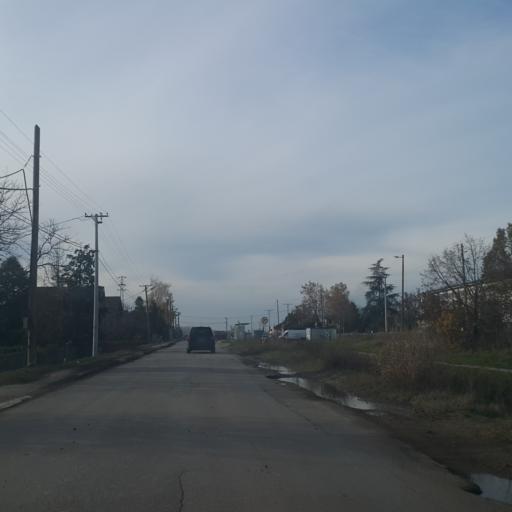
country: RS
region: Central Serbia
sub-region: Belgrade
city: Lazarevac
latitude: 44.3986
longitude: 20.3723
